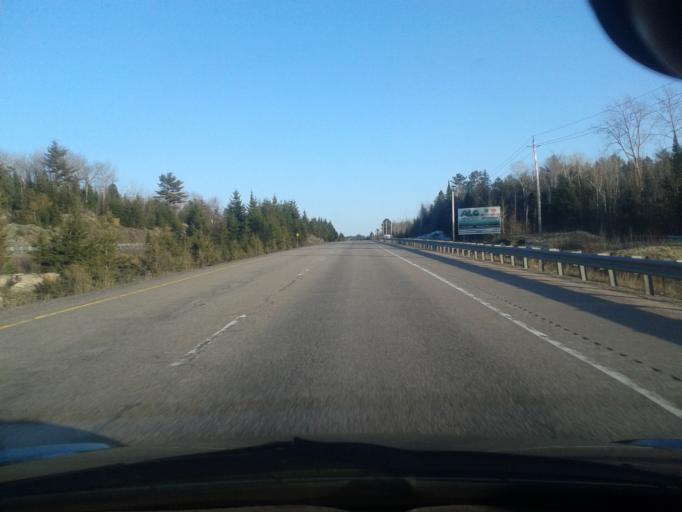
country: CA
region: Ontario
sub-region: Nipissing District
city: North Bay
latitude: 46.2500
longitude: -79.3710
